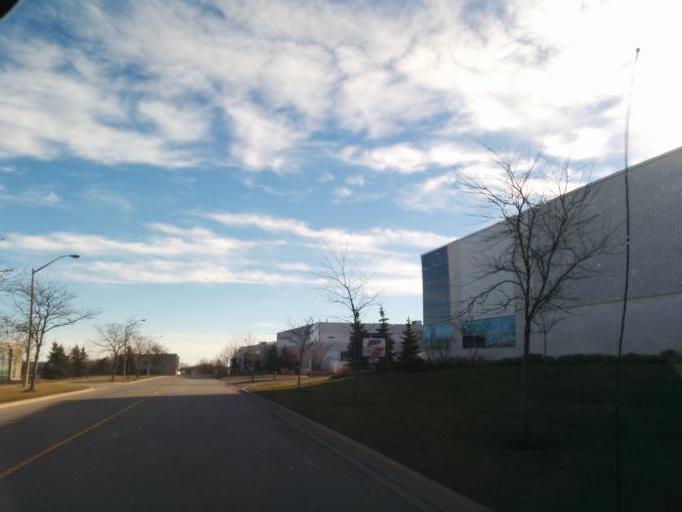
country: CA
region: Ontario
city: Oakville
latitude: 43.5058
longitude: -79.6795
